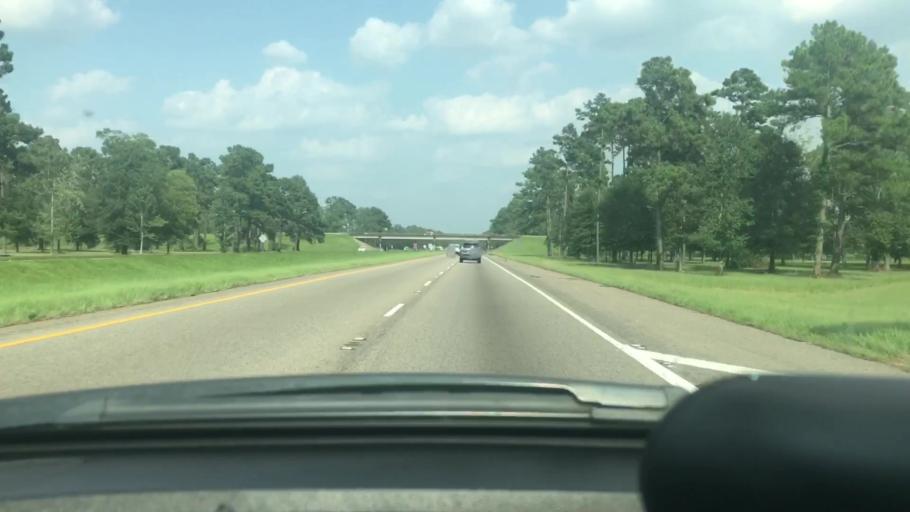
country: US
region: Louisiana
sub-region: Livingston Parish
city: Albany
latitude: 30.4774
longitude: -90.5822
